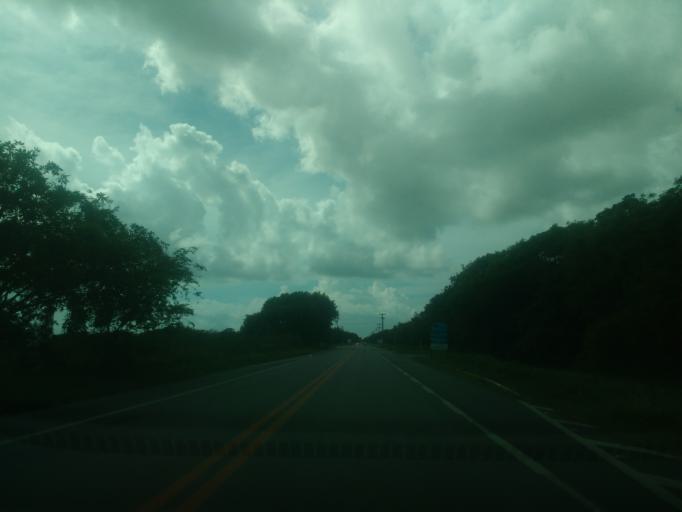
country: BR
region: Alagoas
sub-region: Marechal Deodoro
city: Marechal Deodoro
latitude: -9.6685
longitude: -35.8433
